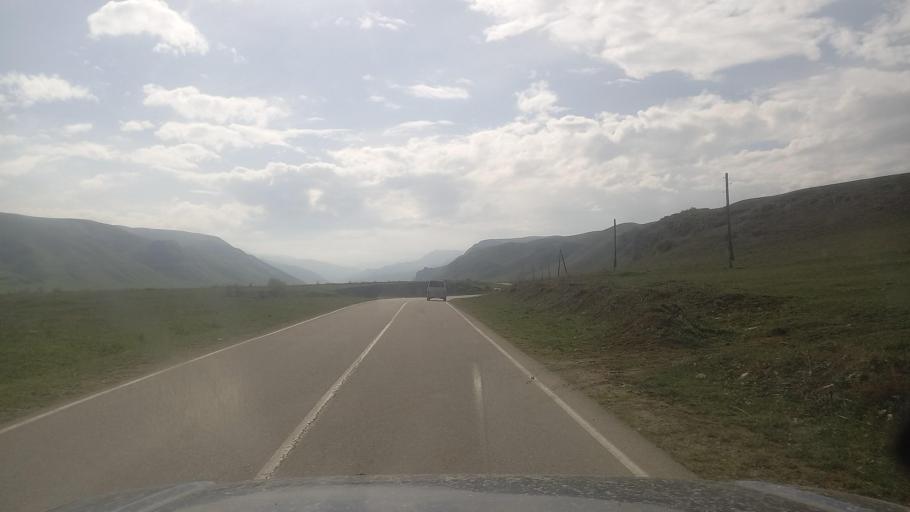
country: RU
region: Kabardino-Balkariya
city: Kamennomostskoye
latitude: 43.7357
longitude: 42.9939
